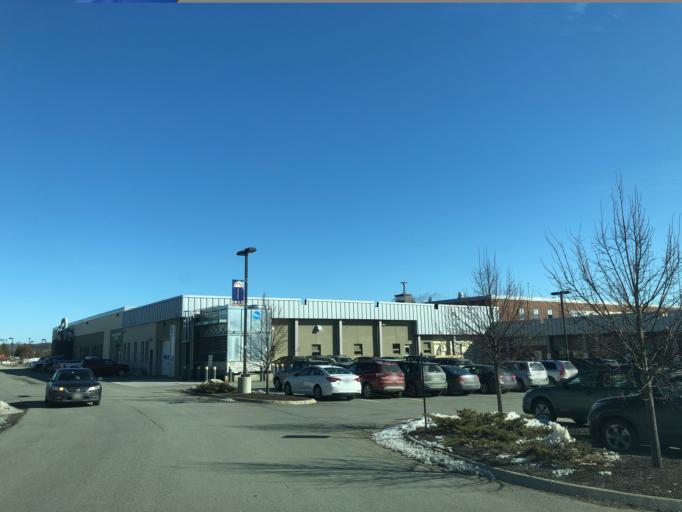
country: US
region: Maine
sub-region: Penobscot County
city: Brewer
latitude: 44.8254
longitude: -68.7447
